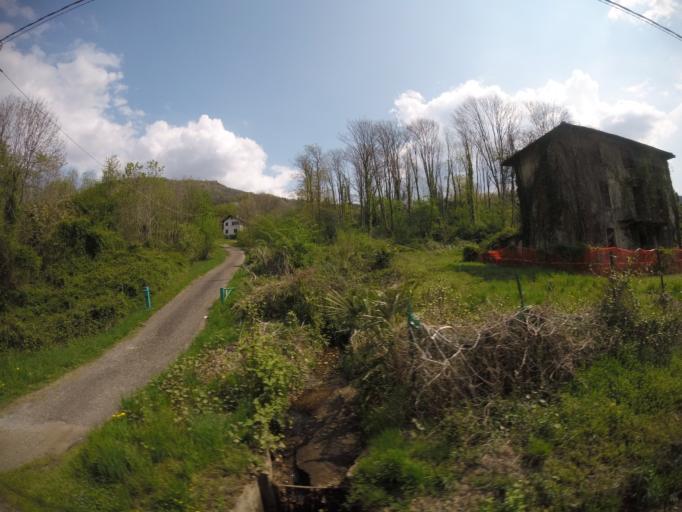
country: IT
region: Piedmont
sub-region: Provincia di Novara
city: Pettenasco
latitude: 45.8241
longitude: 8.4006
